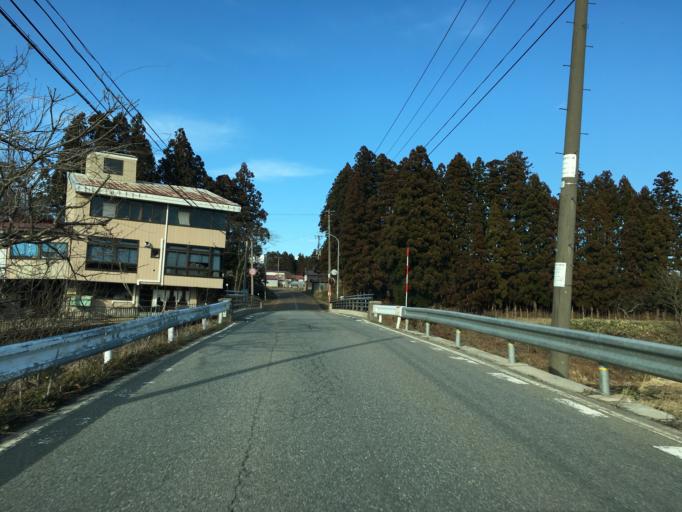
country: JP
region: Yamagata
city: Nagai
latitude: 38.0238
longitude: 139.9763
